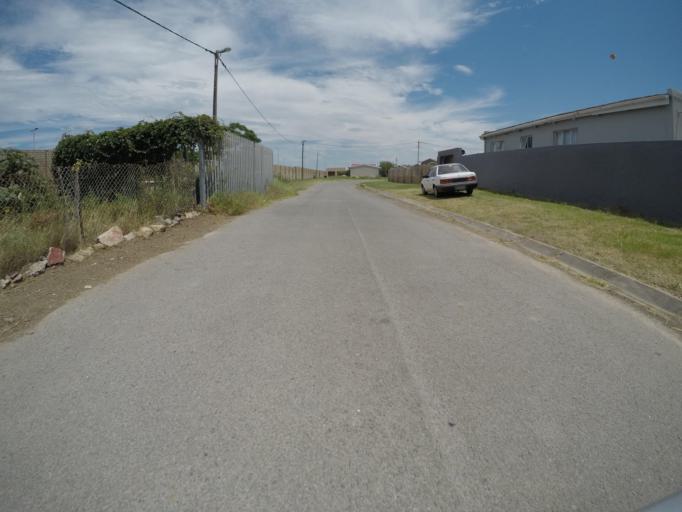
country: ZA
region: Eastern Cape
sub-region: Buffalo City Metropolitan Municipality
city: East London
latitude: -33.0497
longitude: 27.8508
